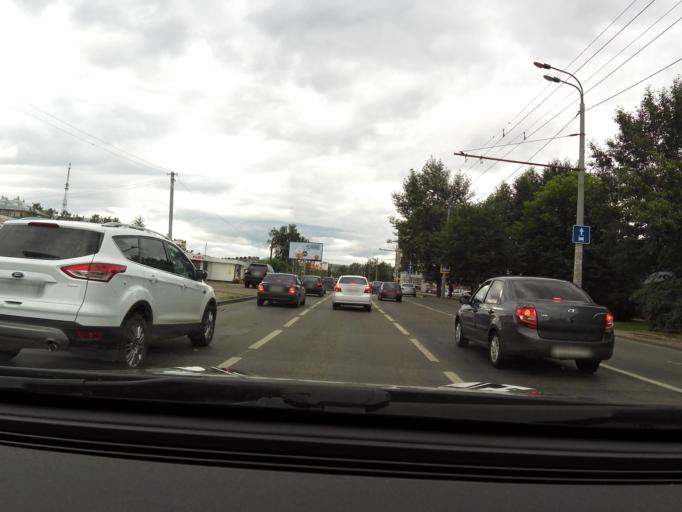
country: RU
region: Tatarstan
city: Staroye Arakchino
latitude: 55.8232
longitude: 49.0472
